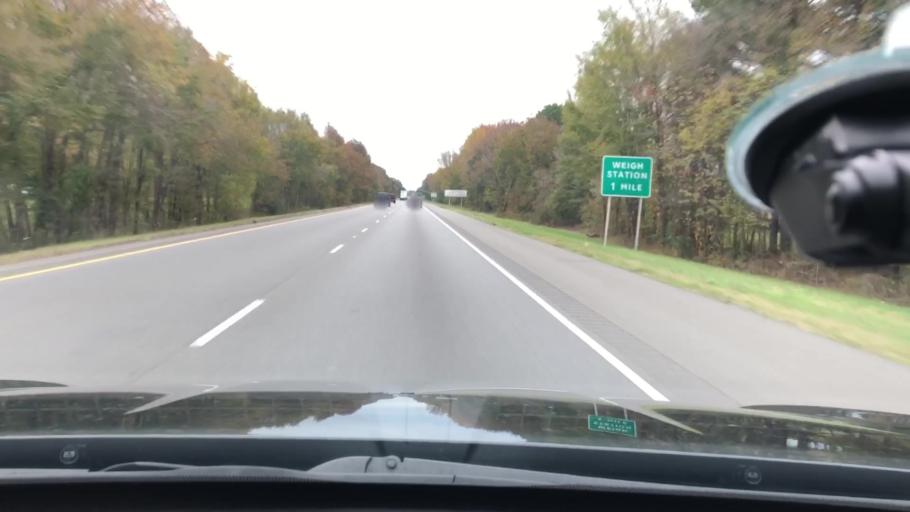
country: US
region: Arkansas
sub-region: Hempstead County
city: Hope
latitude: 33.6429
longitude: -93.6905
